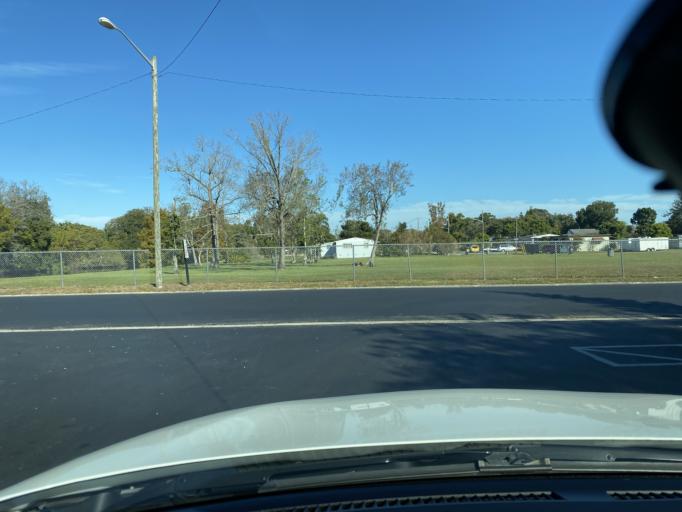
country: US
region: Florida
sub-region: Orange County
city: Azalea Park
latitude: 28.5315
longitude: -81.3123
